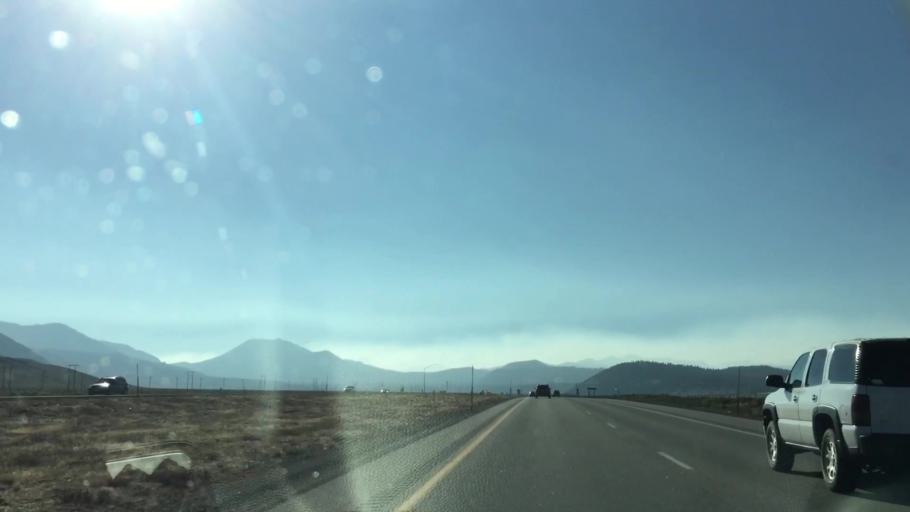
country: US
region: California
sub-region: Mono County
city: Mammoth Lakes
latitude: 37.6218
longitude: -118.8357
